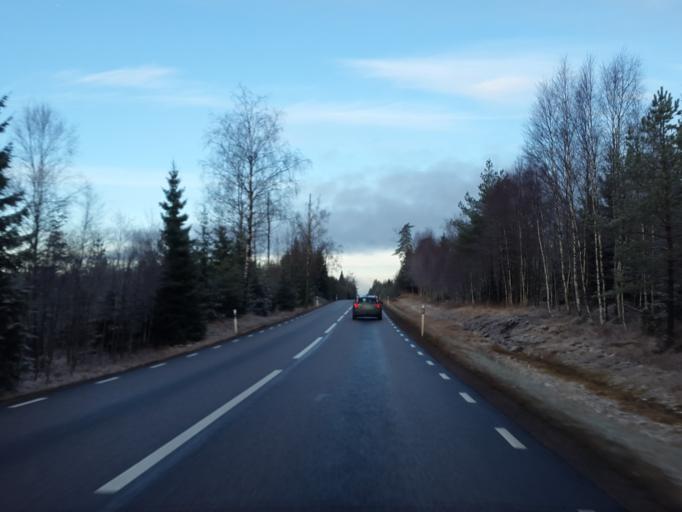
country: SE
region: Vaestra Goetaland
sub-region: Boras Kommun
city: Sjomarken
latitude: 57.7551
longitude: 12.8580
